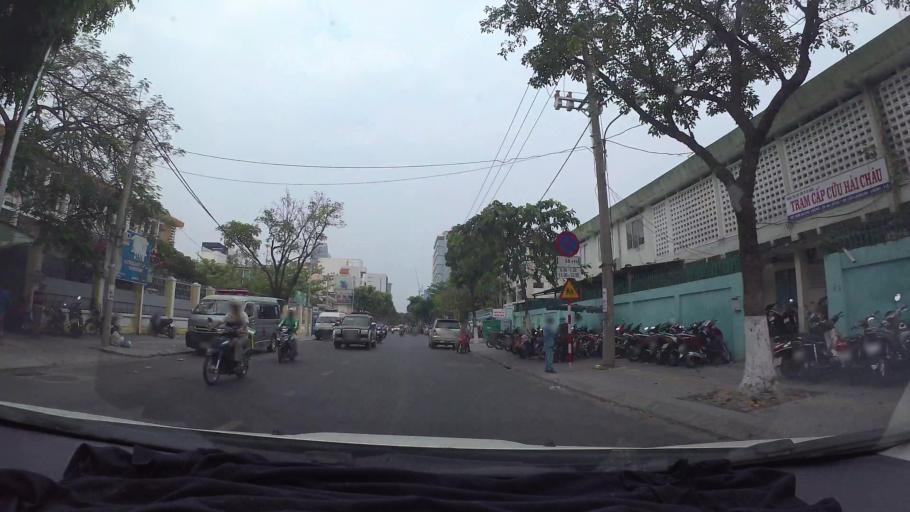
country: VN
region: Da Nang
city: Da Nang
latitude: 16.0739
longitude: 108.2157
